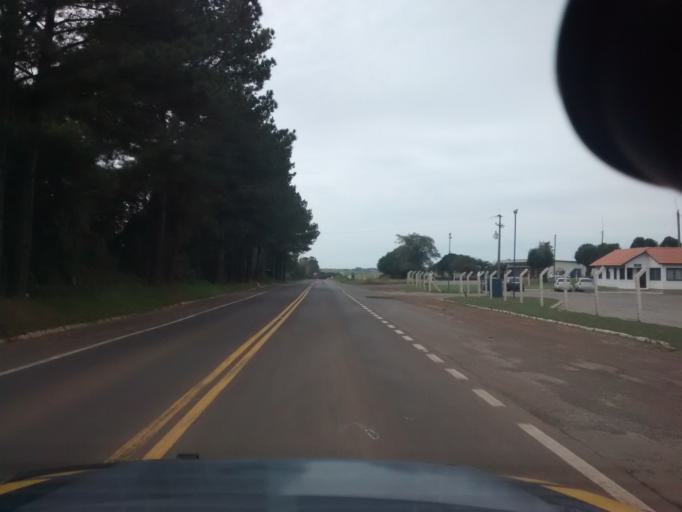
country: BR
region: Rio Grande do Sul
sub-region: Vacaria
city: Vacaria
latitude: -28.4358
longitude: -51.0077
